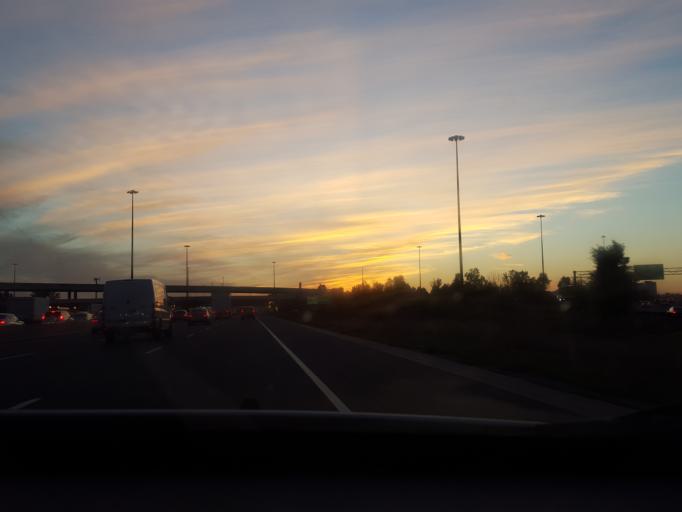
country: CA
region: Ontario
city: Etobicoke
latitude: 43.7172
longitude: -79.5148
